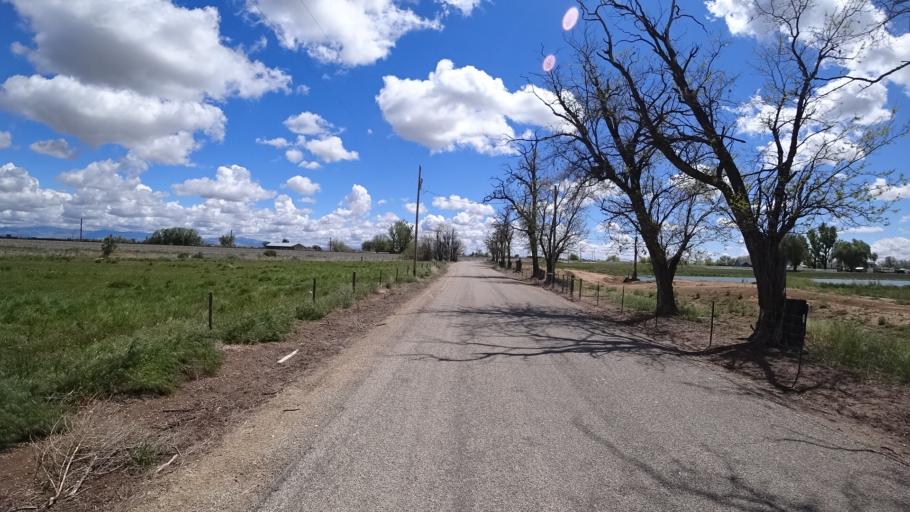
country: US
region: Idaho
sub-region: Ada County
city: Kuna
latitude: 43.4591
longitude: -116.3577
